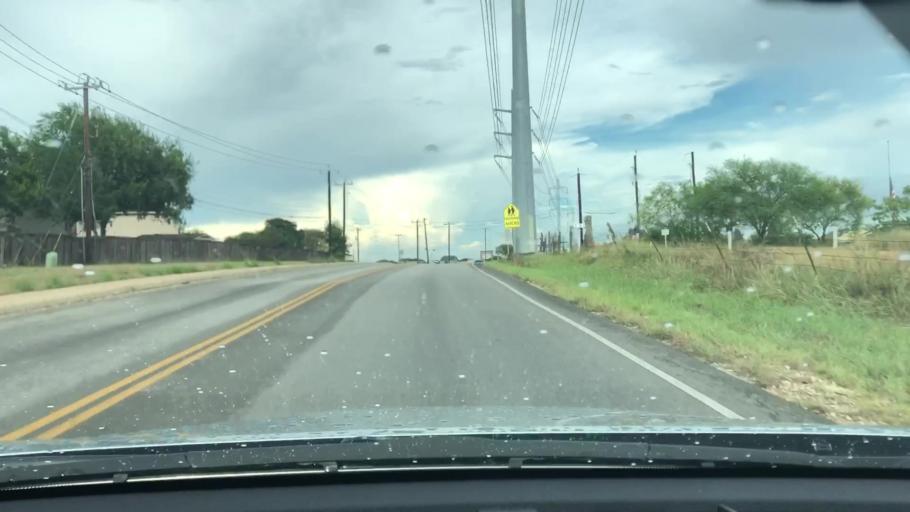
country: US
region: Texas
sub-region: Bexar County
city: Kirby
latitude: 29.4681
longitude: -98.3432
